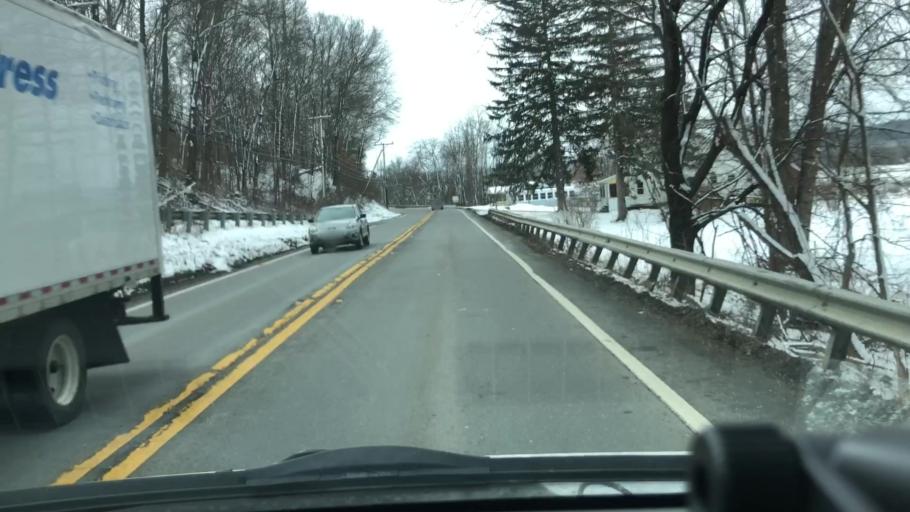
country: US
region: Massachusetts
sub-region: Franklin County
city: Greenfield
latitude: 42.5599
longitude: -72.5957
